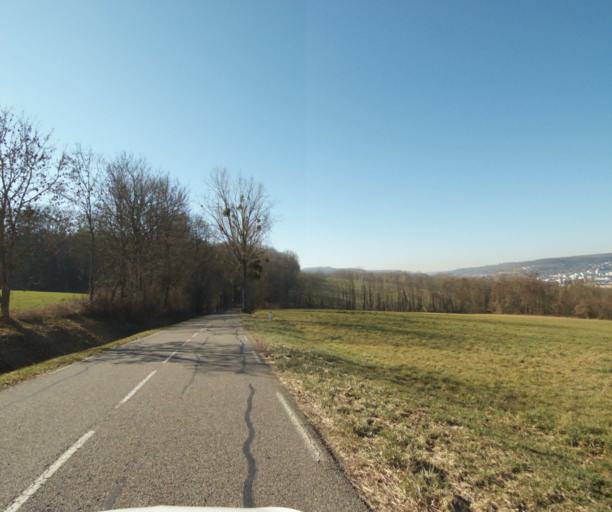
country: FR
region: Lorraine
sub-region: Departement de Meurthe-et-Moselle
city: Lay-Saint-Christophe
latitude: 48.7390
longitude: 6.1890
